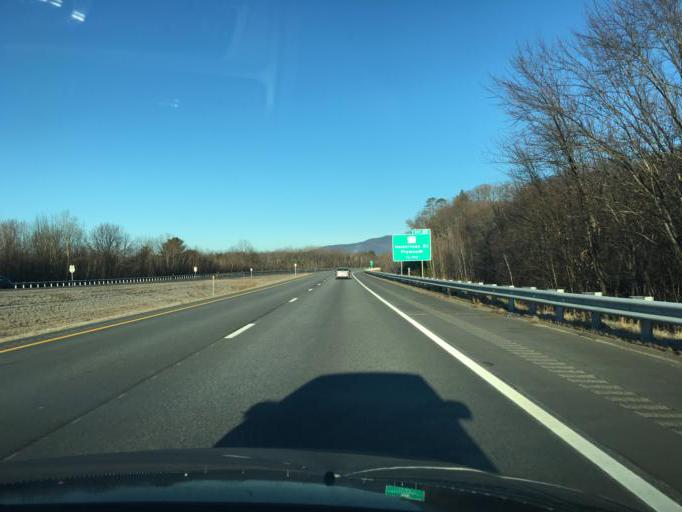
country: US
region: New Hampshire
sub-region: Grafton County
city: Plymouth
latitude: 43.7542
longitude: -71.6724
